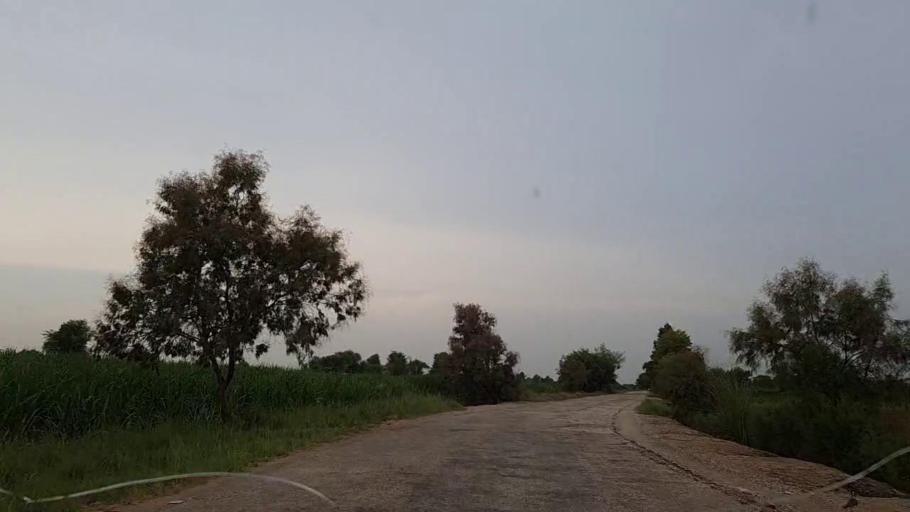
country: PK
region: Sindh
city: Mirpur Mathelo
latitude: 27.8859
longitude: 69.6393
